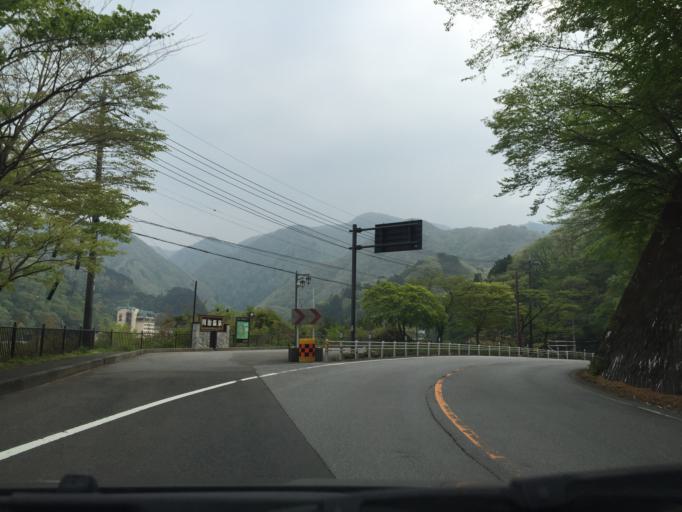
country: JP
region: Tochigi
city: Nikko
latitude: 36.8889
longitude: 139.7052
